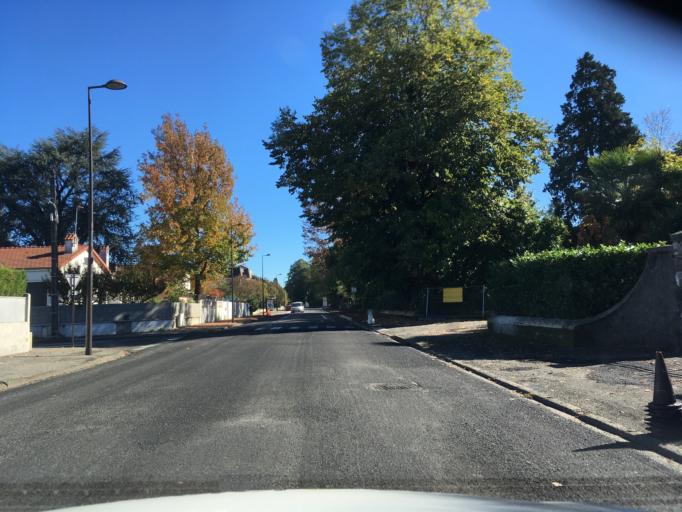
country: FR
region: Aquitaine
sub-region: Departement des Pyrenees-Atlantiques
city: Bizanos
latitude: 43.2985
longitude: -0.3430
